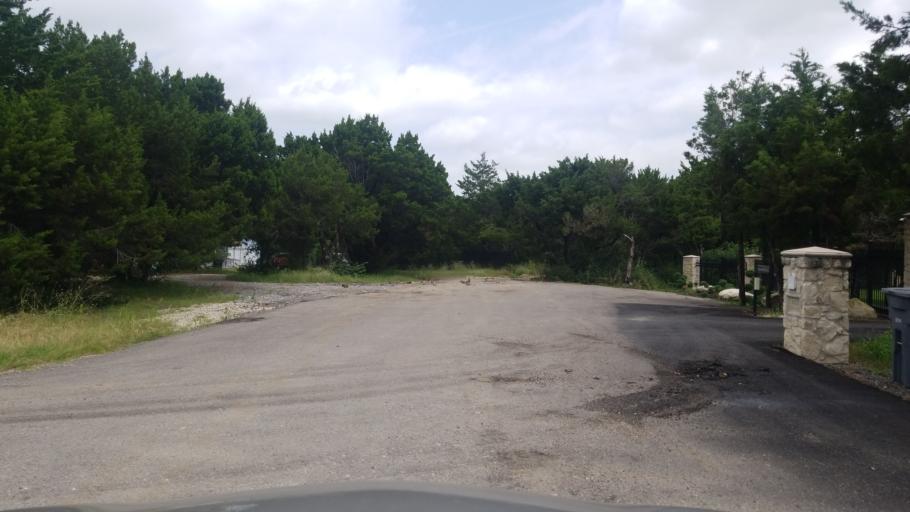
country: US
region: Texas
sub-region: Dallas County
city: Duncanville
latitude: 32.6846
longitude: -96.9312
